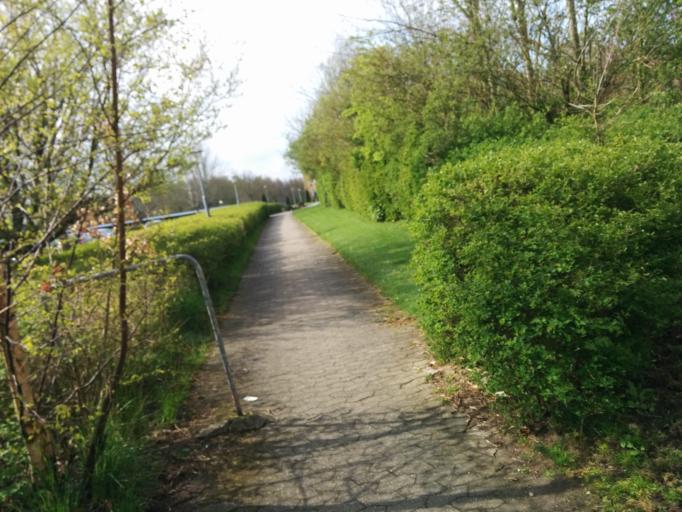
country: DK
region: Central Jutland
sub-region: Viborg Kommune
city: Viborg
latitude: 56.4392
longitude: 9.3855
